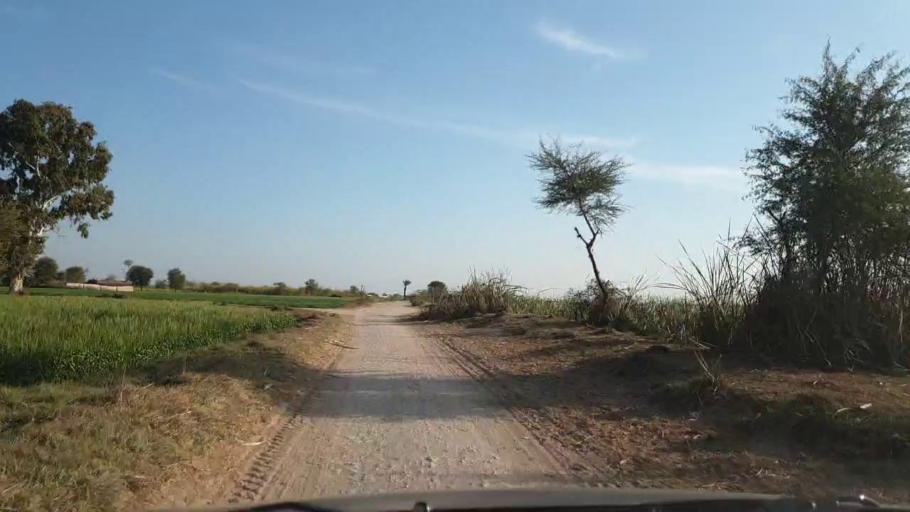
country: PK
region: Sindh
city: Khadro
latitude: 26.2127
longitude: 68.7434
